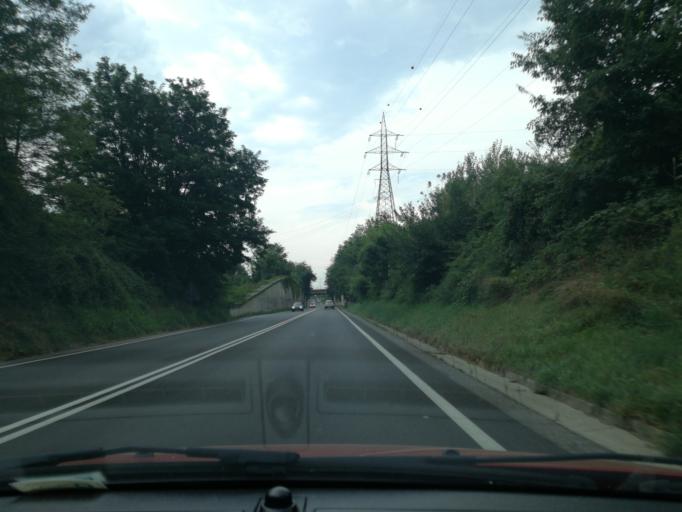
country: IT
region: Lombardy
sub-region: Provincia di Monza e Brianza
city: Velasca
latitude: 45.6394
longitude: 9.3475
